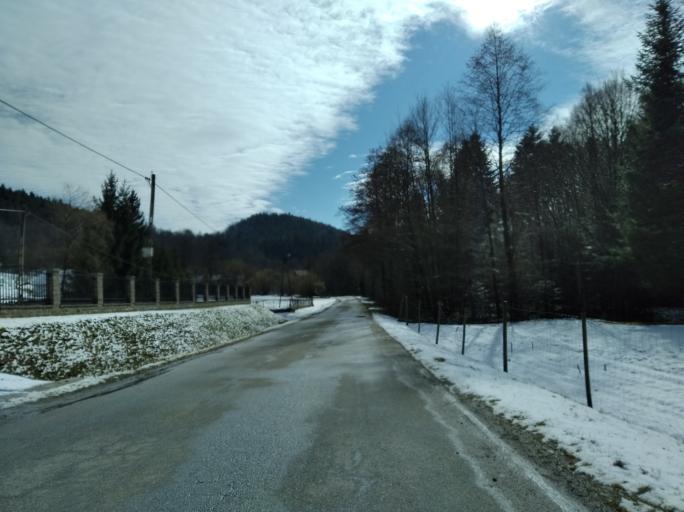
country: PL
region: Subcarpathian Voivodeship
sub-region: Powiat brzozowski
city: Jablonica Polska
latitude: 49.7450
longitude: 21.8833
